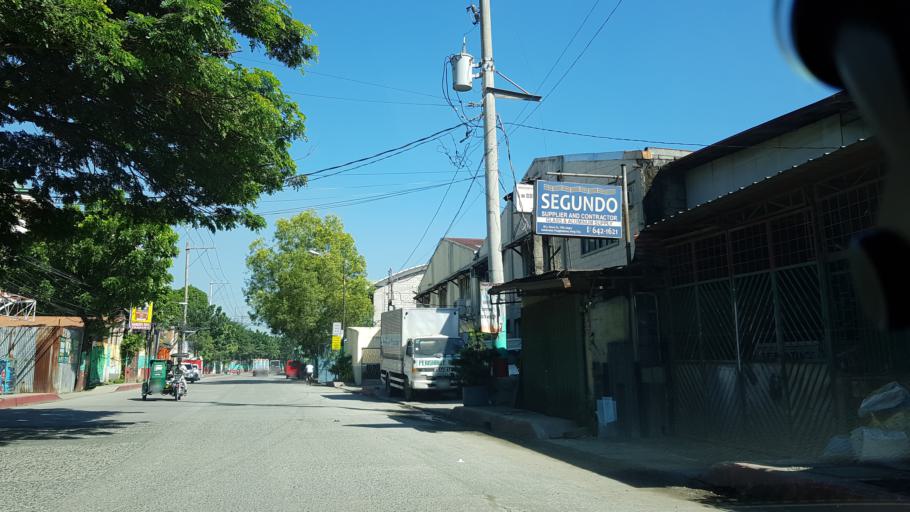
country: PH
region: Calabarzon
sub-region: Province of Rizal
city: Pateros
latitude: 14.5588
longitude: 121.0961
